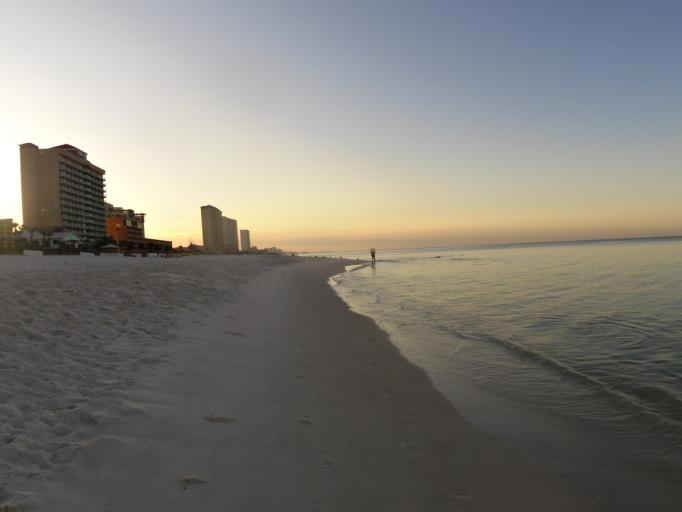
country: US
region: Florida
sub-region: Bay County
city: Laguna Beach
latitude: 30.2100
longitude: -85.8683
